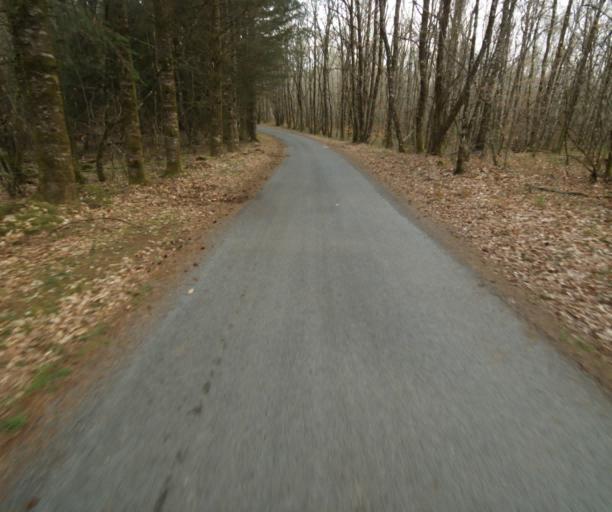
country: FR
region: Limousin
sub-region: Departement de la Correze
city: Correze
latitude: 45.2728
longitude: 1.9523
